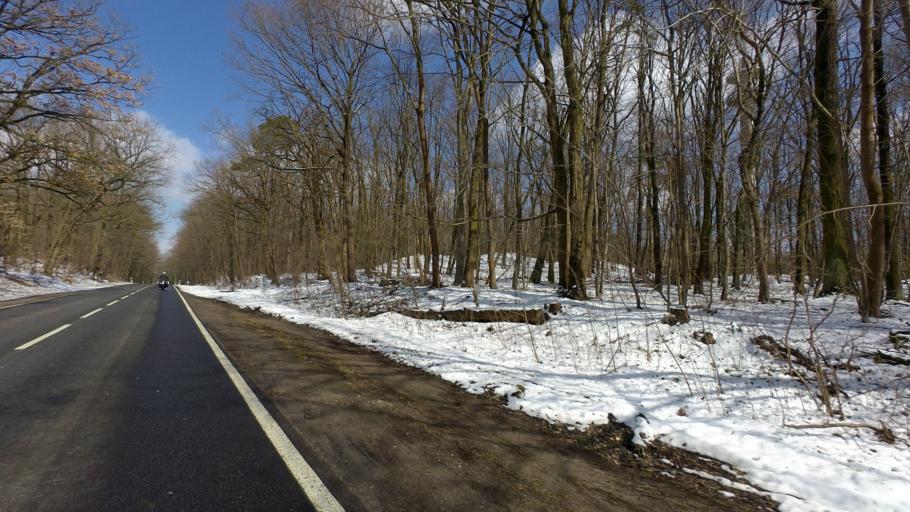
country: DE
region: Brandenburg
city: Eberswalde
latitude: 52.8228
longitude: 13.8316
